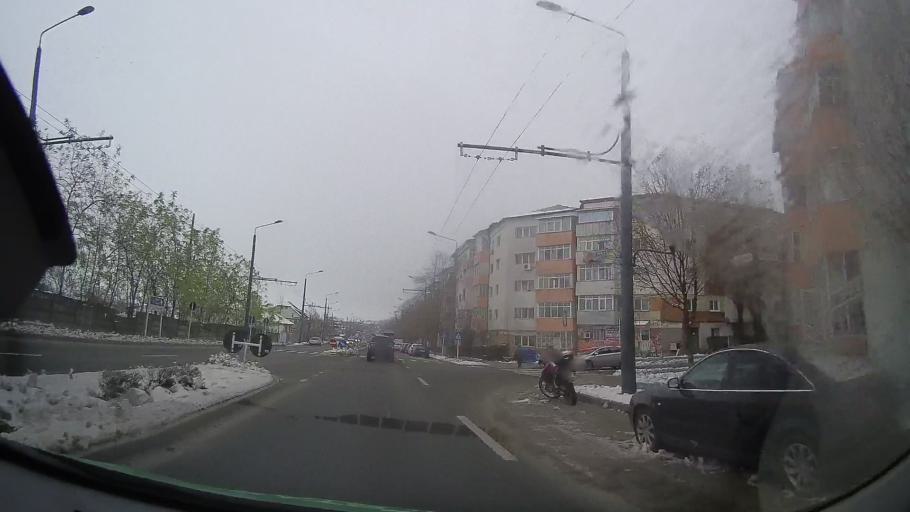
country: RO
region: Vaslui
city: Vaslui
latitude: 46.6515
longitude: 27.7356
